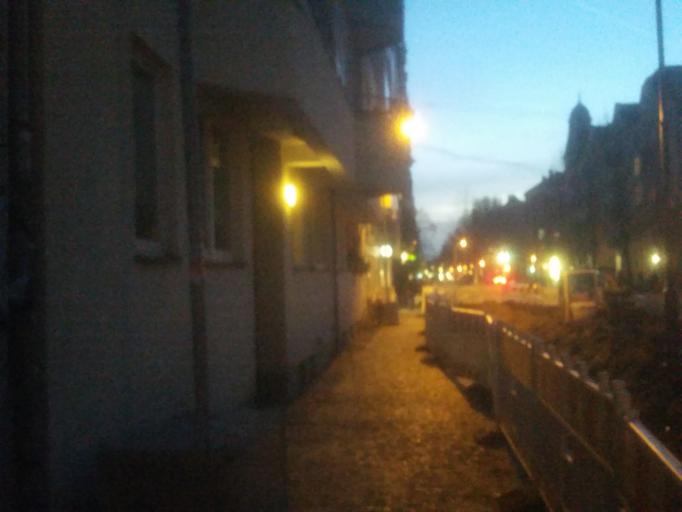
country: DE
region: Berlin
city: Prenzlauer Berg Bezirk
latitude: 52.5451
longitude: 13.4169
